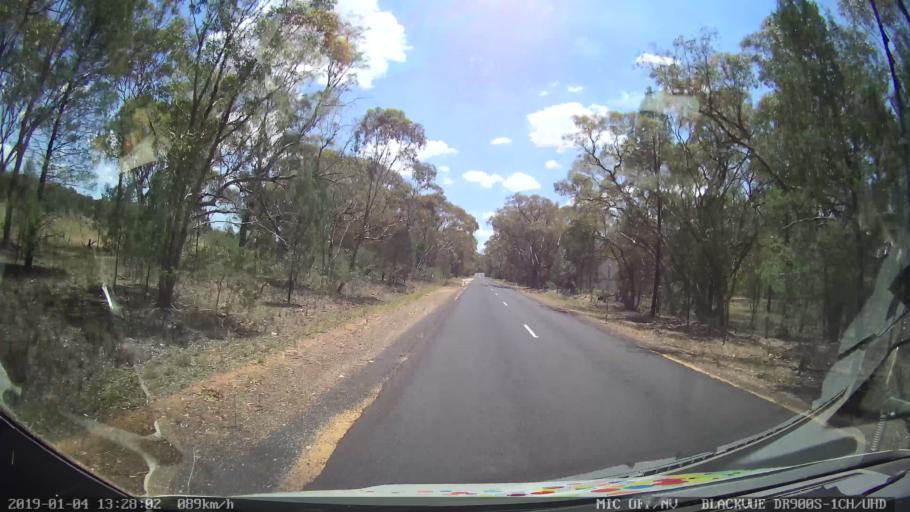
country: AU
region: New South Wales
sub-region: Parkes
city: Peak Hill
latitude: -32.6617
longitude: 148.5566
